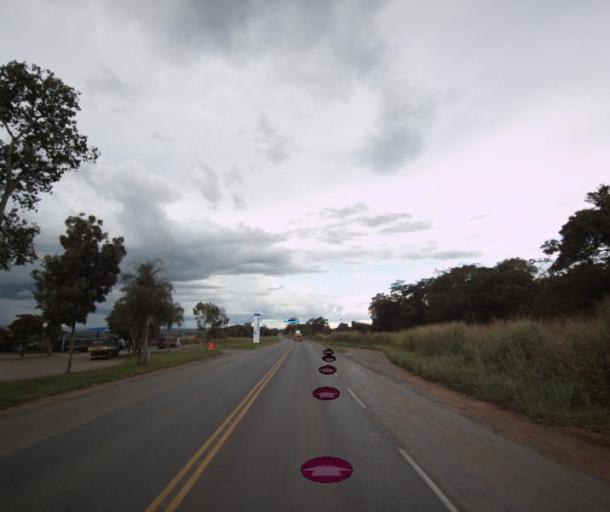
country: BR
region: Goias
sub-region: Itapaci
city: Itapaci
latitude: -15.0246
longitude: -49.4276
